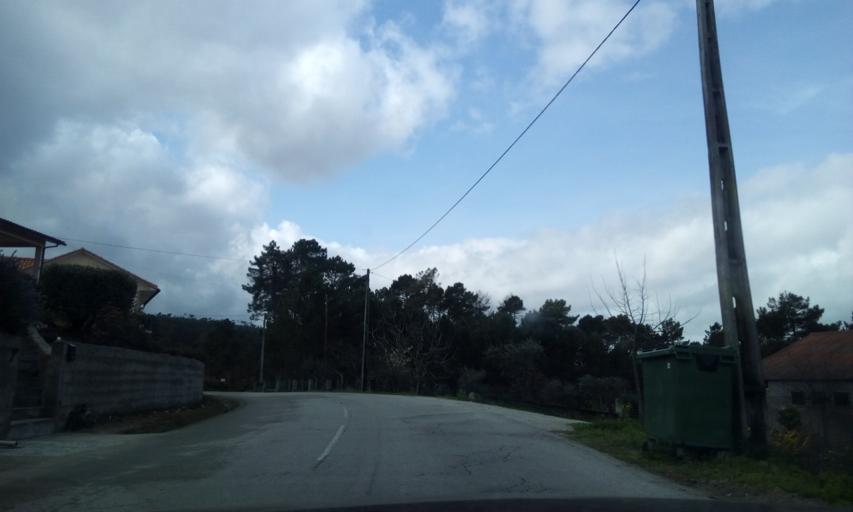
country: PT
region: Guarda
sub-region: Fornos de Algodres
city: Fornos de Algodres
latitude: 40.6684
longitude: -7.6128
